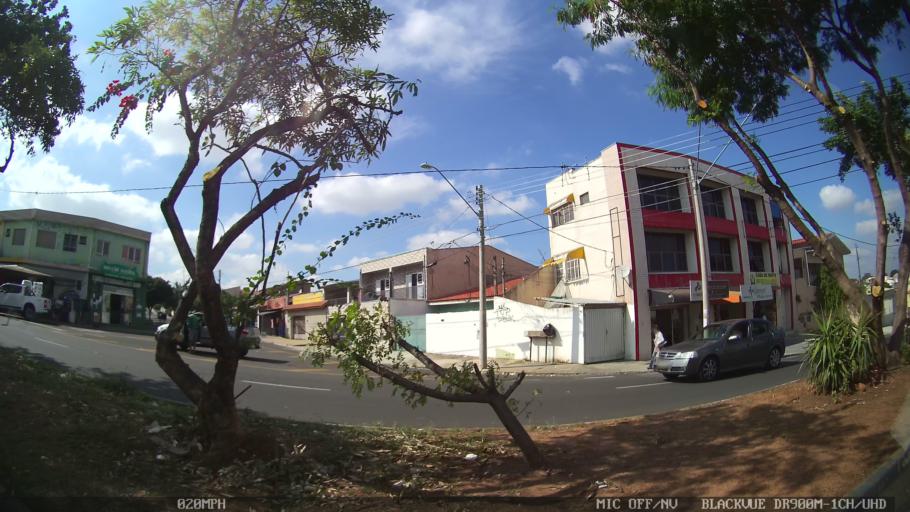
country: BR
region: Sao Paulo
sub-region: Campinas
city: Campinas
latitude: -22.9379
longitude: -47.1195
